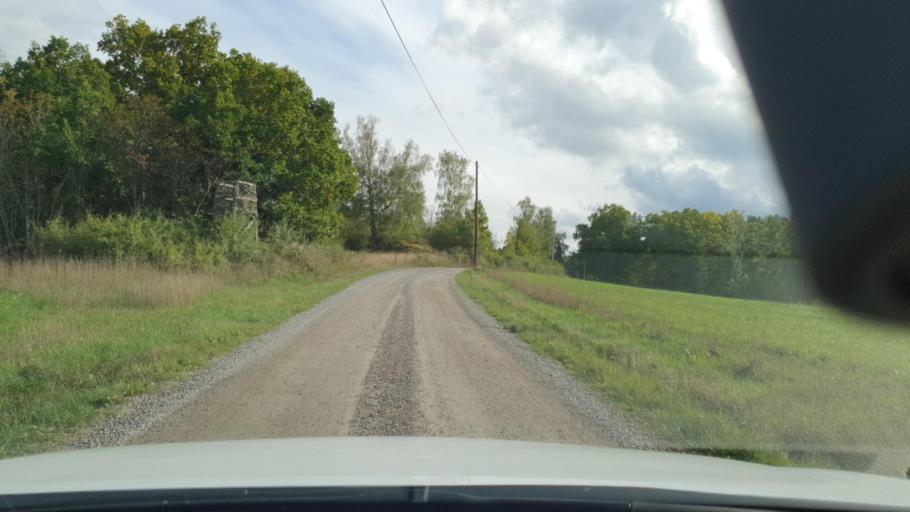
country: SE
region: Kalmar
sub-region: Vasterviks Kommun
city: Ankarsrum
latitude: 57.7050
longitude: 16.4529
